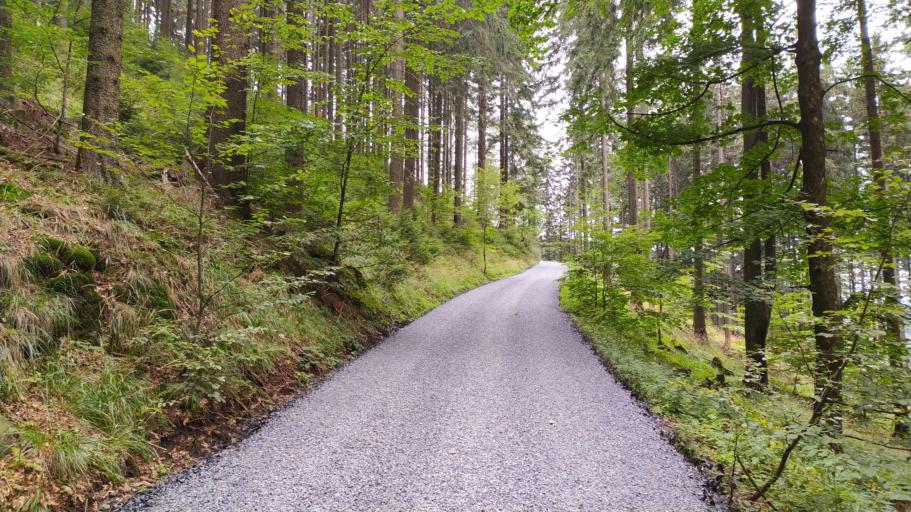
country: CZ
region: Moravskoslezsky
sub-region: Okres Frydek-Mistek
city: Celadna
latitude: 49.5075
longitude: 18.3491
